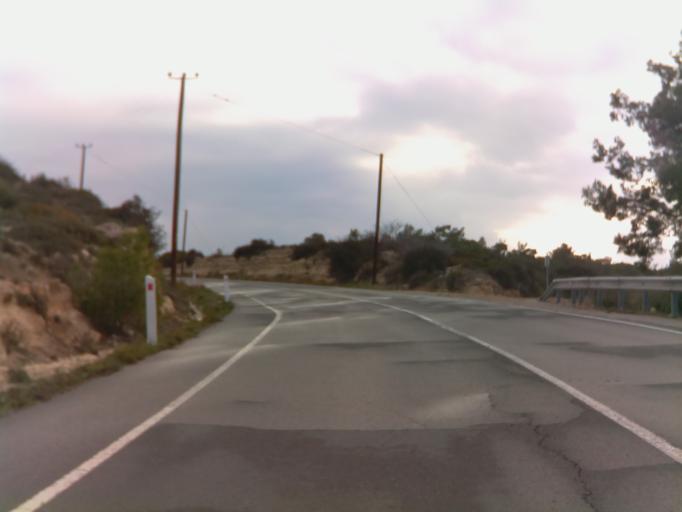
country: CY
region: Pafos
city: Pegeia
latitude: 34.8949
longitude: 32.3792
